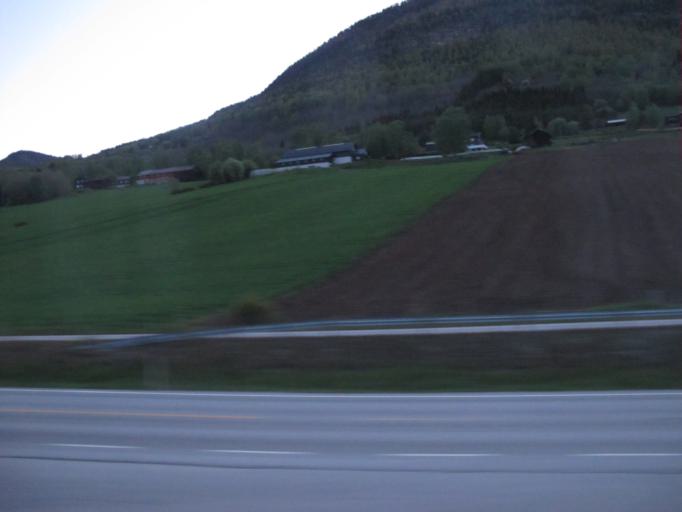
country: NO
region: Oppland
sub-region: Nord-Fron
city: Vinstra
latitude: 61.6658
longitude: 9.7122
